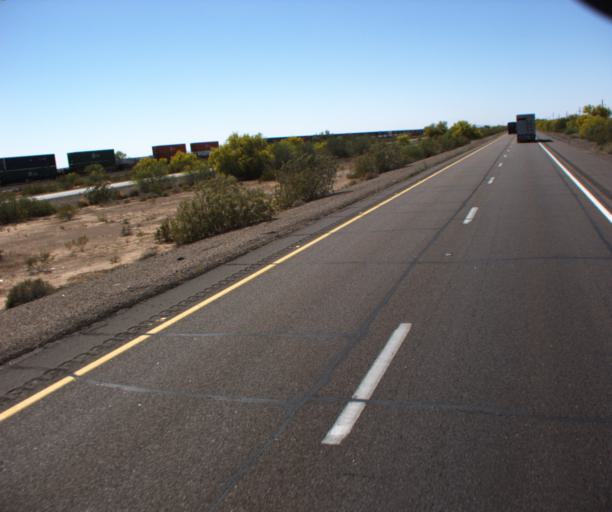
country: US
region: Arizona
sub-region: Maricopa County
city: Gila Bend
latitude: 32.8432
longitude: -113.3006
